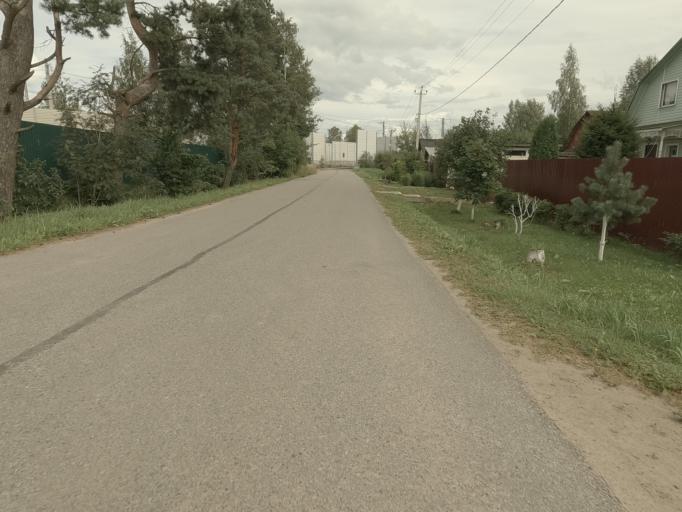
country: RU
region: Leningrad
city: Mga
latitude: 59.7597
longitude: 31.0365
